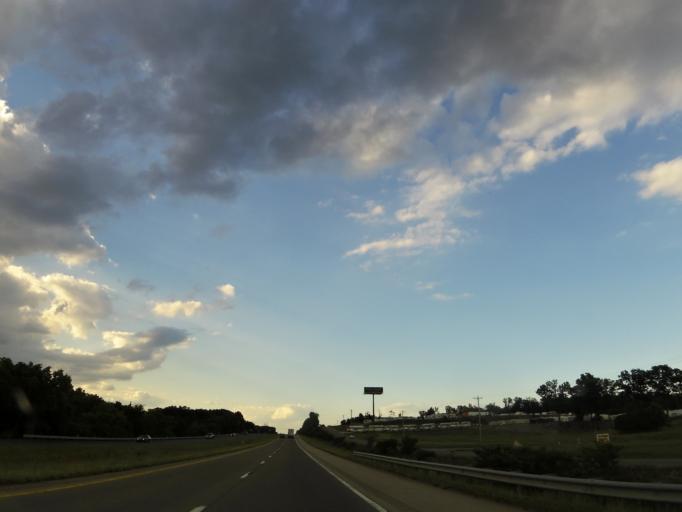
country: US
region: Tennessee
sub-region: Maury County
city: Spring Hill
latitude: 35.6962
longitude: -86.8838
